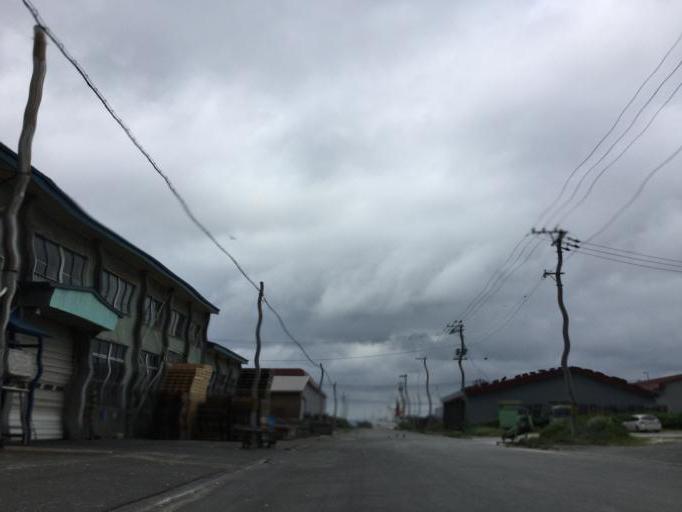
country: JP
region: Hokkaido
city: Wakkanai
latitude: 45.4066
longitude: 141.6802
